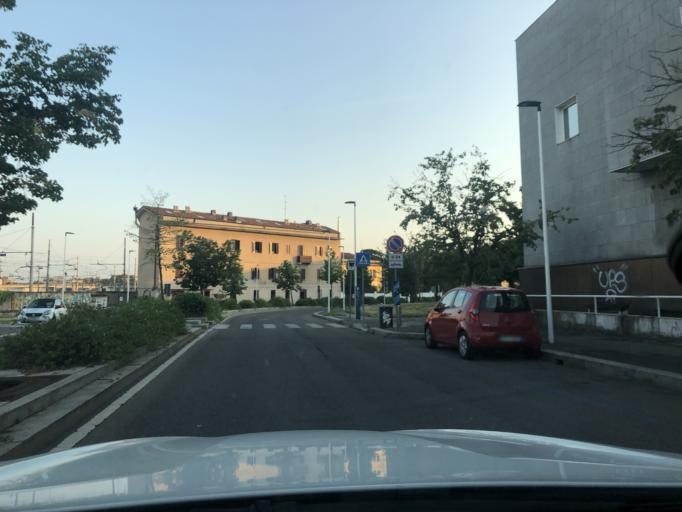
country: IT
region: Lombardy
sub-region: Citta metropolitana di Milano
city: Sesto San Giovanni
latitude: 45.5103
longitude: 9.2121
